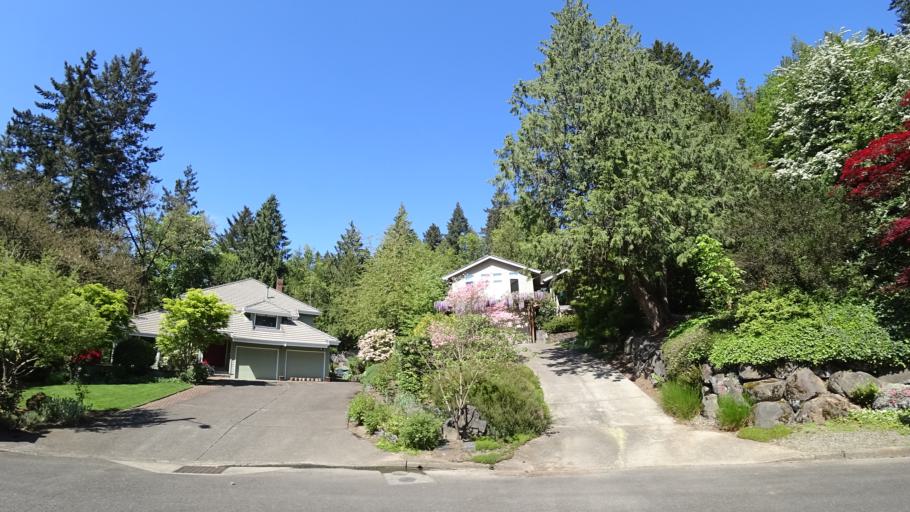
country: US
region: Oregon
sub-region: Washington County
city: West Slope
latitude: 45.4992
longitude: -122.7433
